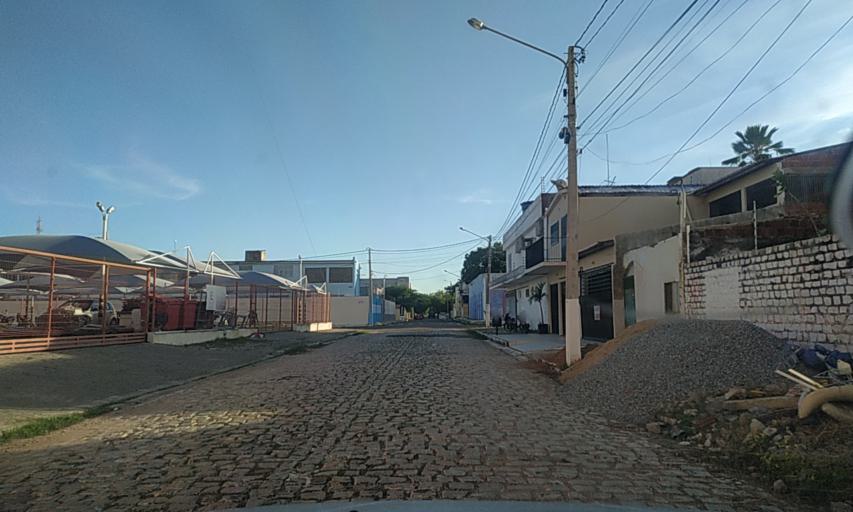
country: BR
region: Rio Grande do Norte
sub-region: Mossoro
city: Mossoro
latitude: -5.1903
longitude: -37.3372
